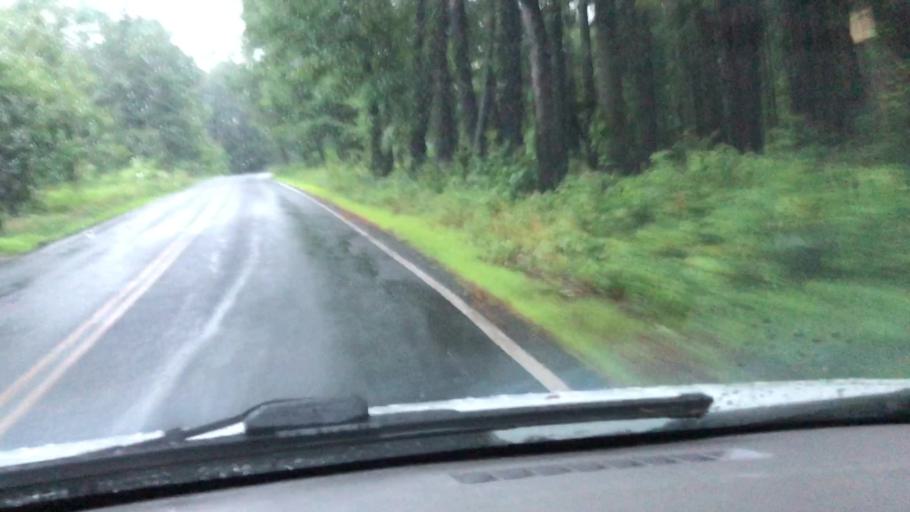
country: US
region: Massachusetts
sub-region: Hampshire County
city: Westhampton
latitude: 42.2802
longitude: -72.7546
